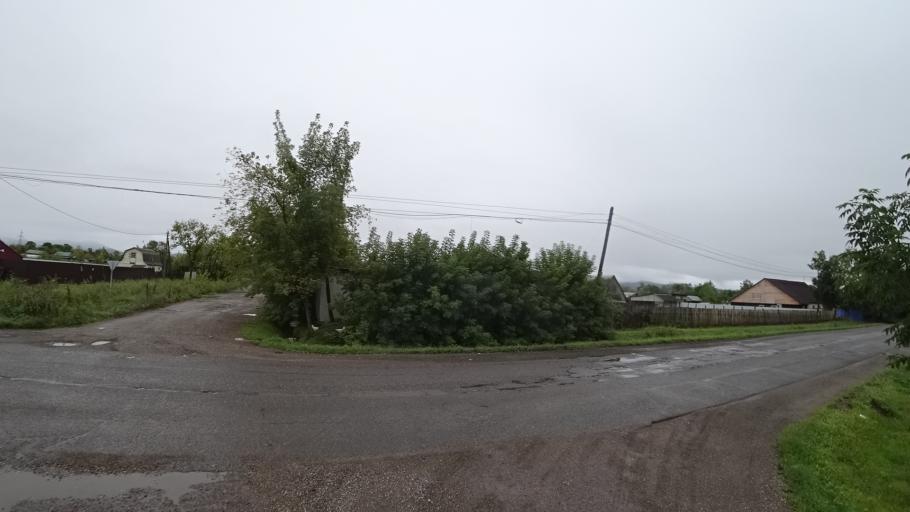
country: RU
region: Primorskiy
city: Monastyrishche
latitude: 44.2001
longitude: 132.4651
